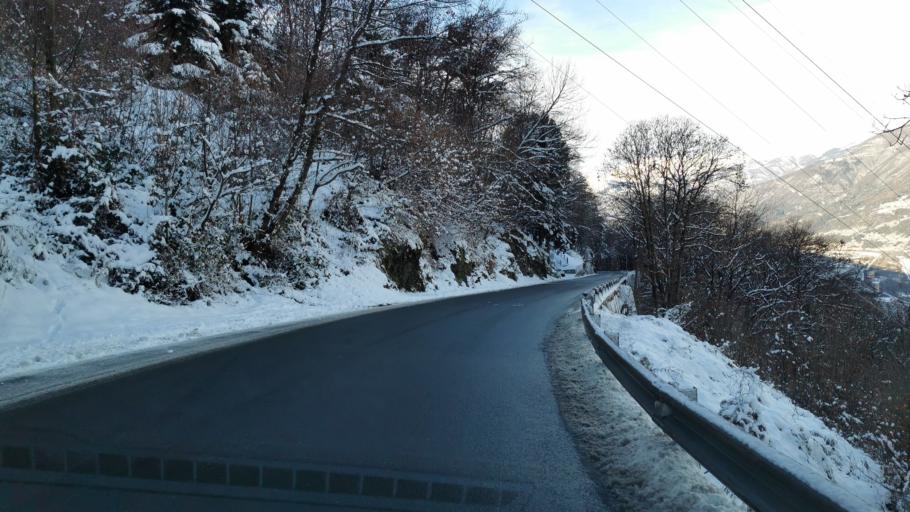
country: IT
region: Lombardy
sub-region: Provincia di Sondrio
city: Regoledo
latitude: 46.1233
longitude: 9.5504
